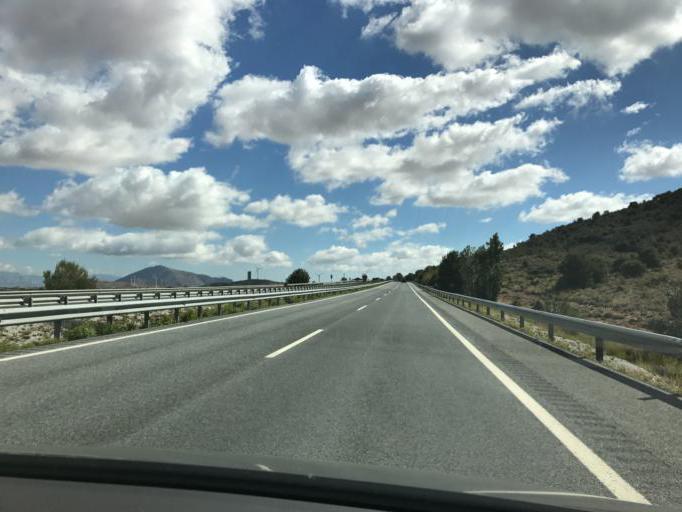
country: ES
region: Andalusia
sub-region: Provincia de Granada
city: Freila
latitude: 37.4668
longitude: -2.8639
